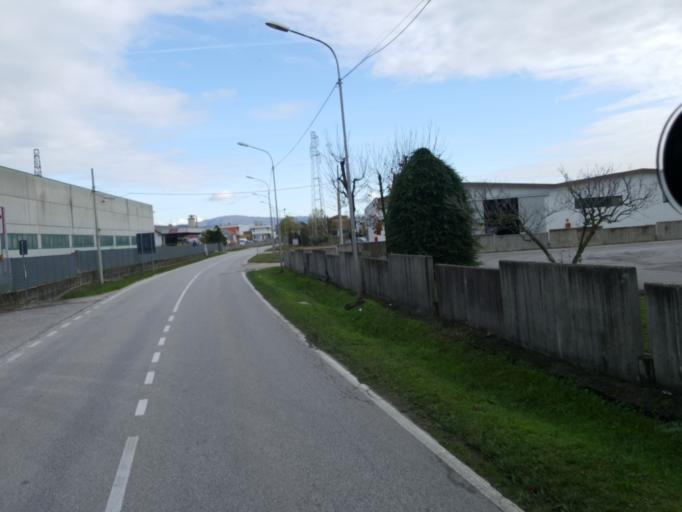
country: IT
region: Friuli Venezia Giulia
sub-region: Provincia di Udine
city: Manzano
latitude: 45.9802
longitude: 13.3574
